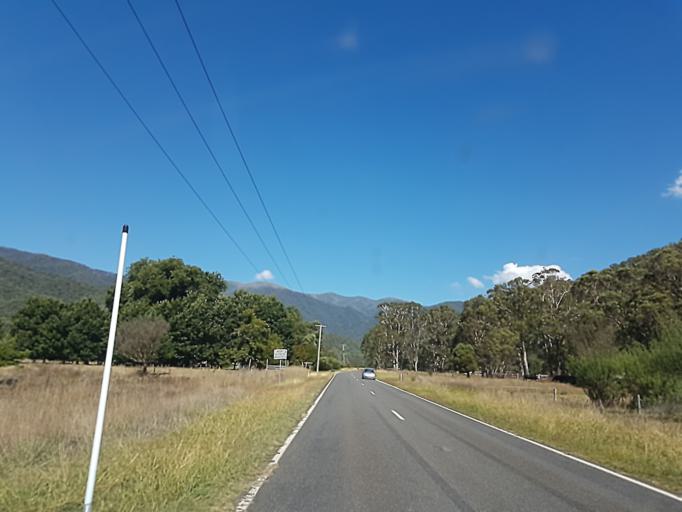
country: AU
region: Victoria
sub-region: Alpine
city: Mount Beauty
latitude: -36.8303
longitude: 147.0725
